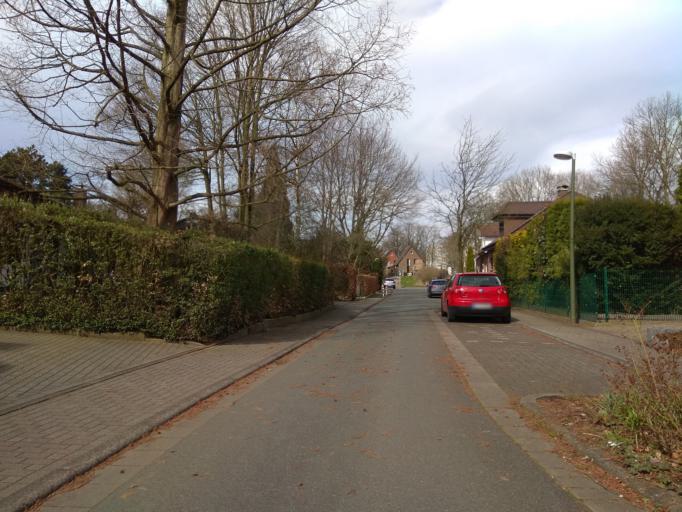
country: DE
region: North Rhine-Westphalia
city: Marl
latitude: 51.6482
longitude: 7.0796
